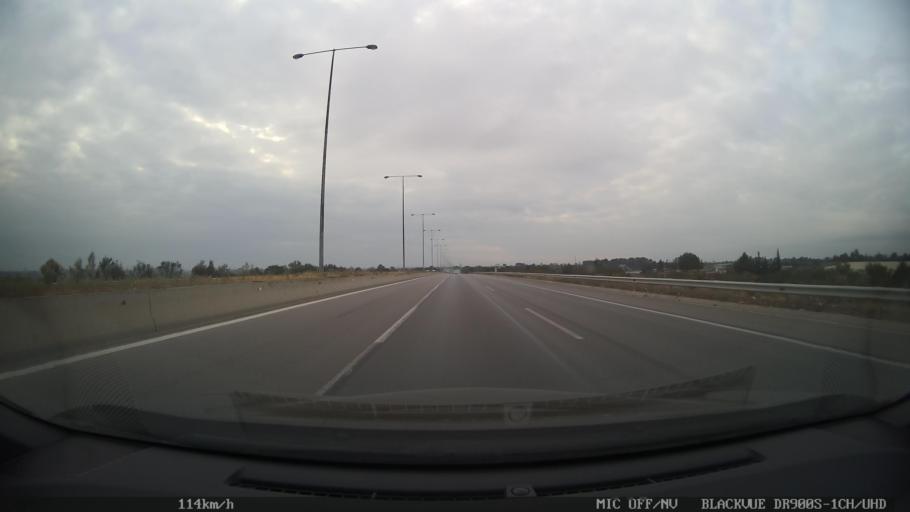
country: GR
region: Central Macedonia
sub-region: Nomos Thessalonikis
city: Nea Magnisia
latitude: 40.6670
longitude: 22.8355
